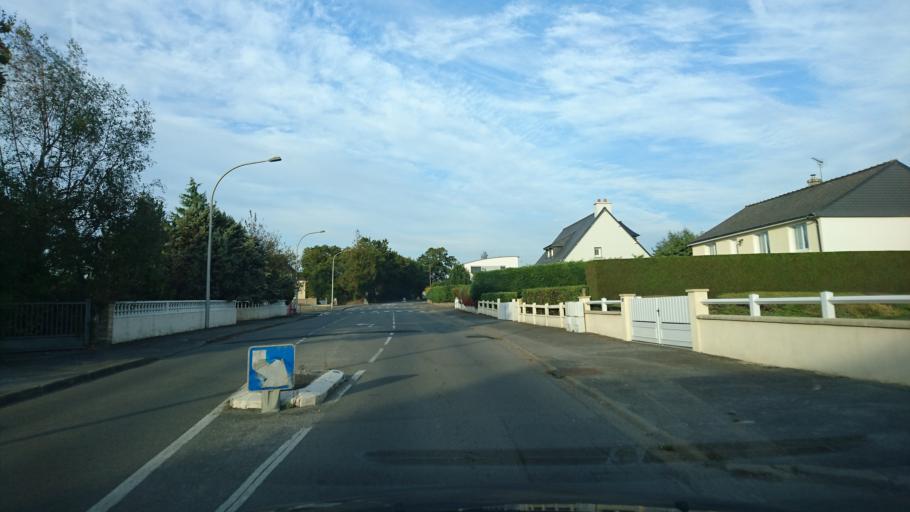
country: FR
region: Pays de la Loire
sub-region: Departement de la Loire-Atlantique
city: Saint-Nicolas-de-Redon
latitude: 47.6586
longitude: -2.0691
